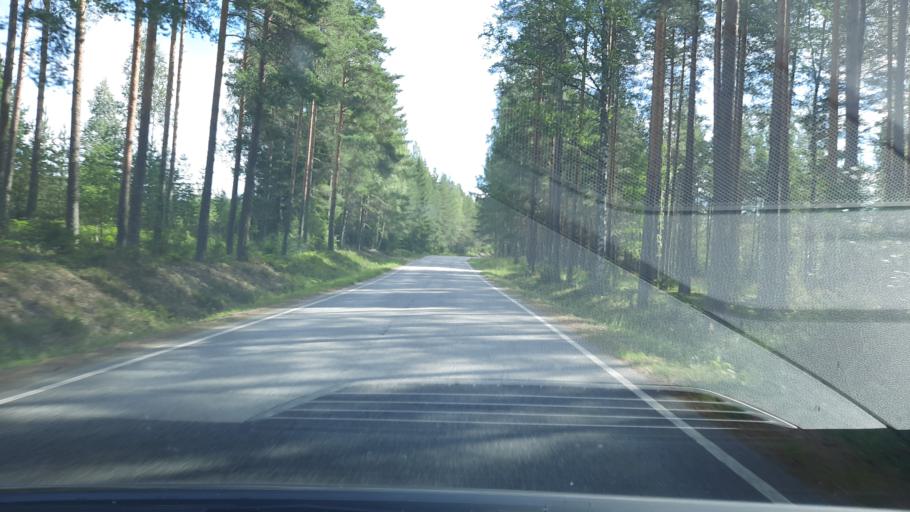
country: FI
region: Pirkanmaa
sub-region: Etelae-Pirkanmaa
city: Urjala
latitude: 61.1720
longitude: 23.3834
